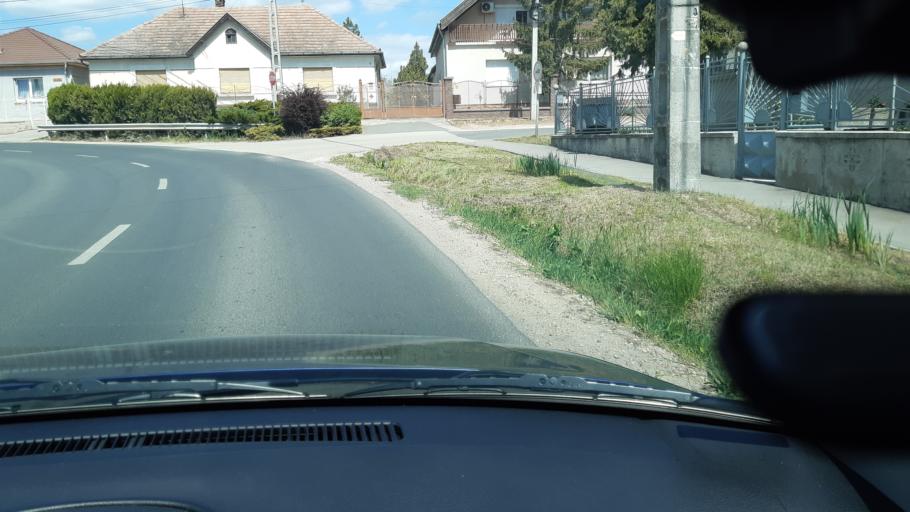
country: HU
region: Pest
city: Nagytarcsa
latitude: 47.5305
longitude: 19.2832
